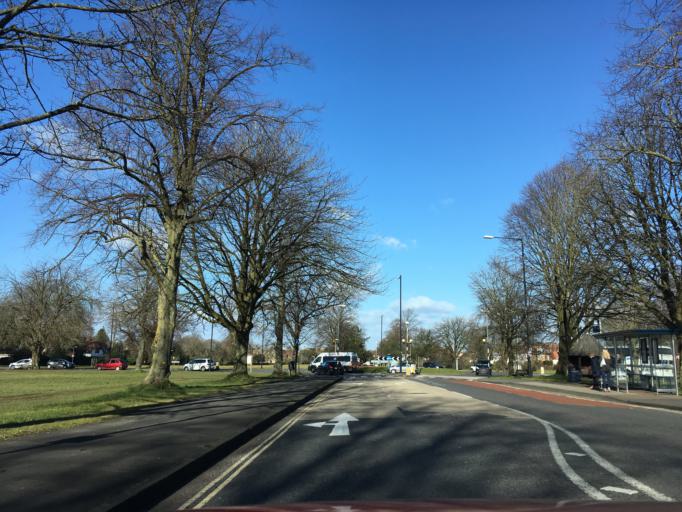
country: GB
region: England
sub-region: Bristol
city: Bristol
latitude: 51.4786
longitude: -2.6168
